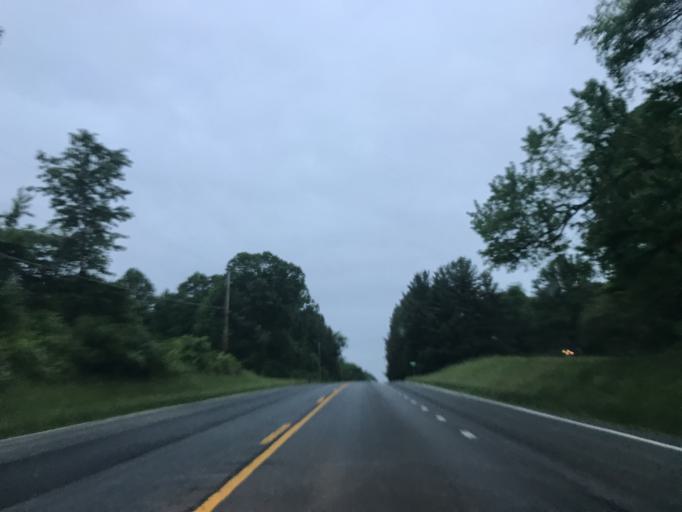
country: US
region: Maryland
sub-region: Frederick County
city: Linganore
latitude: 39.4140
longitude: -77.2545
